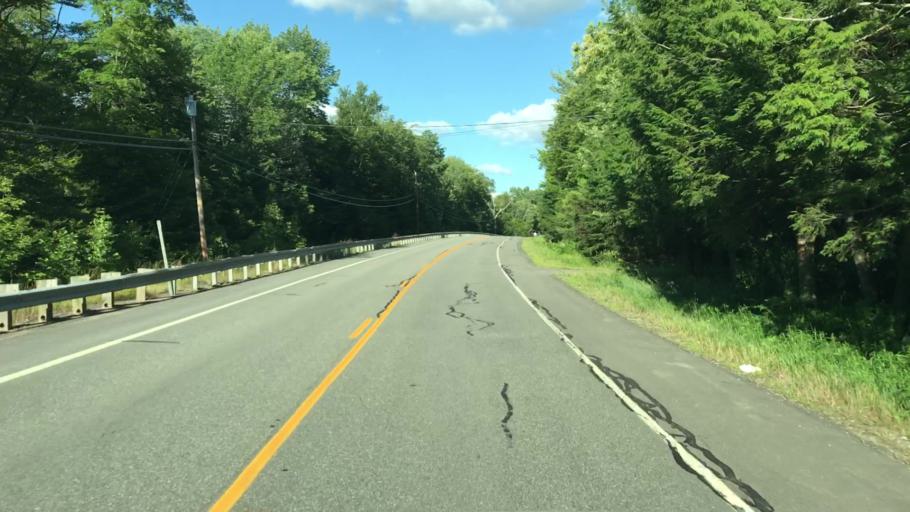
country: US
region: Maine
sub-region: Penobscot County
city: Lincoln
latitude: 45.3789
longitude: -68.4518
